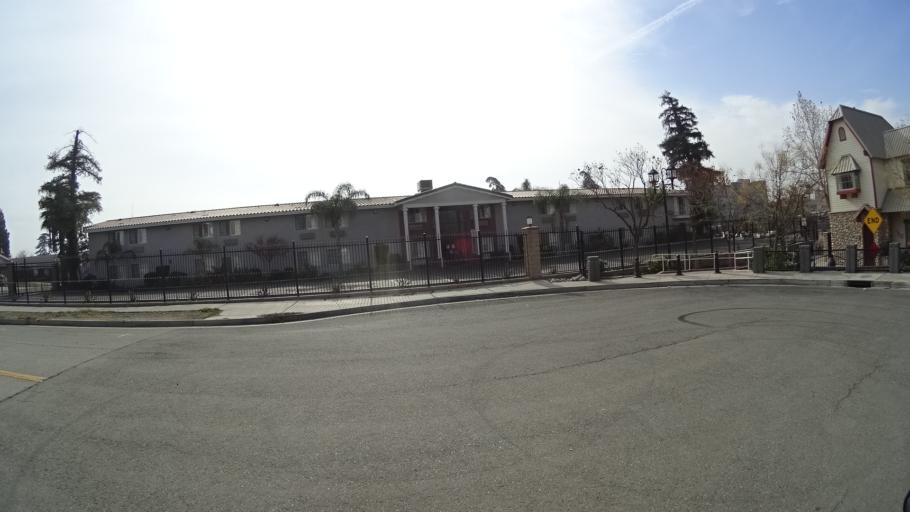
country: US
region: California
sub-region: Kern County
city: Bakersfield
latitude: 35.3744
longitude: -119.0087
